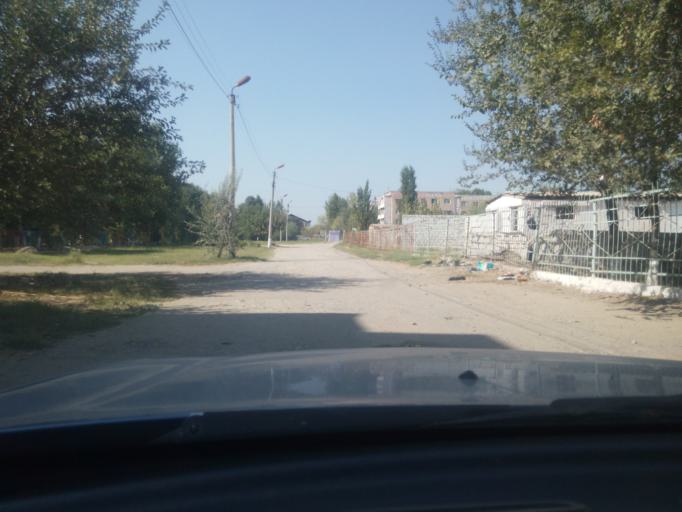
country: UZ
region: Sirdaryo
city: Guliston
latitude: 40.5162
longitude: 68.7777
